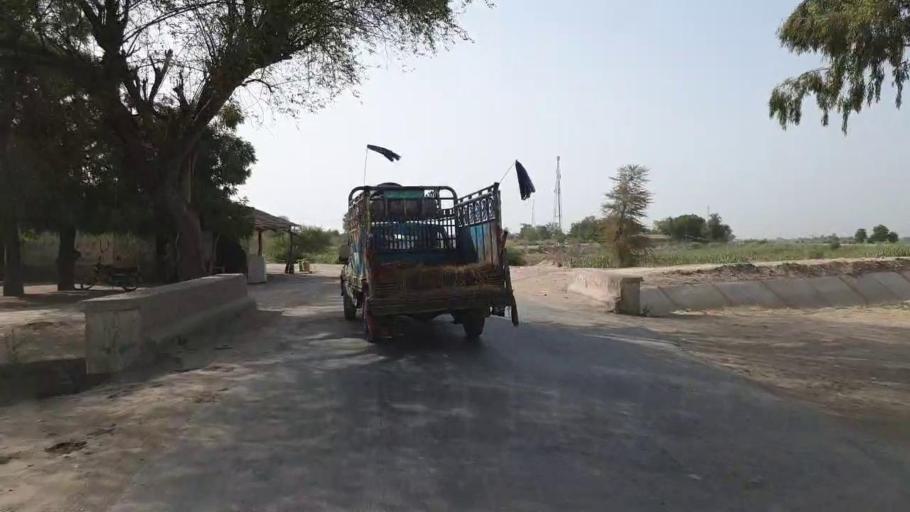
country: PK
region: Sindh
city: Sanghar
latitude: 26.2640
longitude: 68.9298
